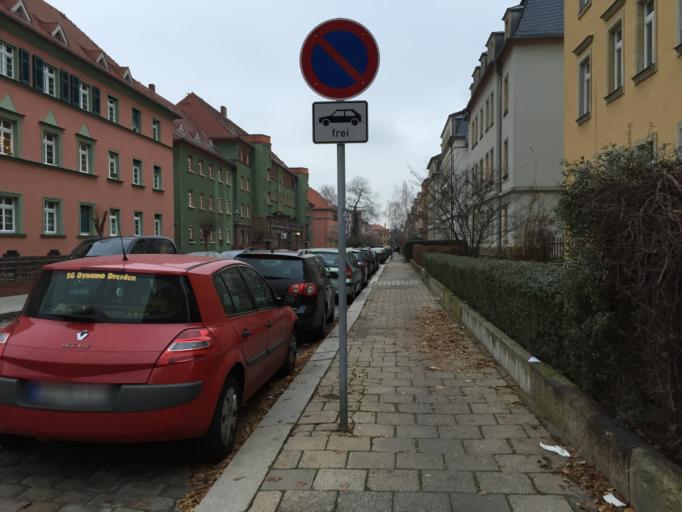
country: DE
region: Saxony
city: Dresden
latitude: 51.0395
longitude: 13.6930
